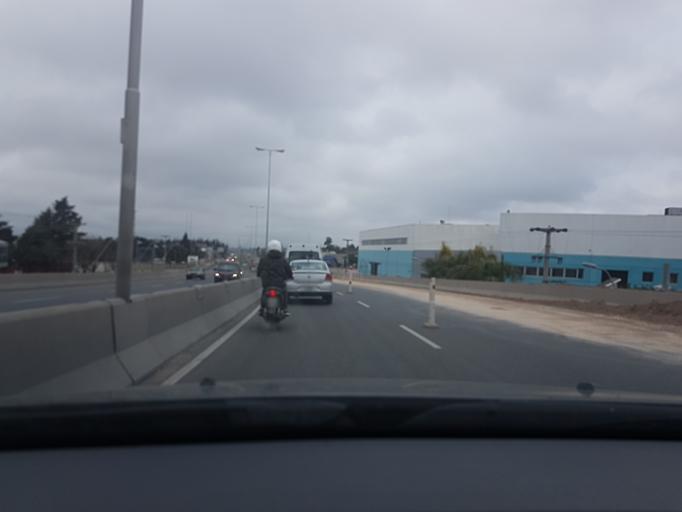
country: AR
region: Cordoba
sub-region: Departamento de Capital
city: Cordoba
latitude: -31.3438
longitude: -64.2076
